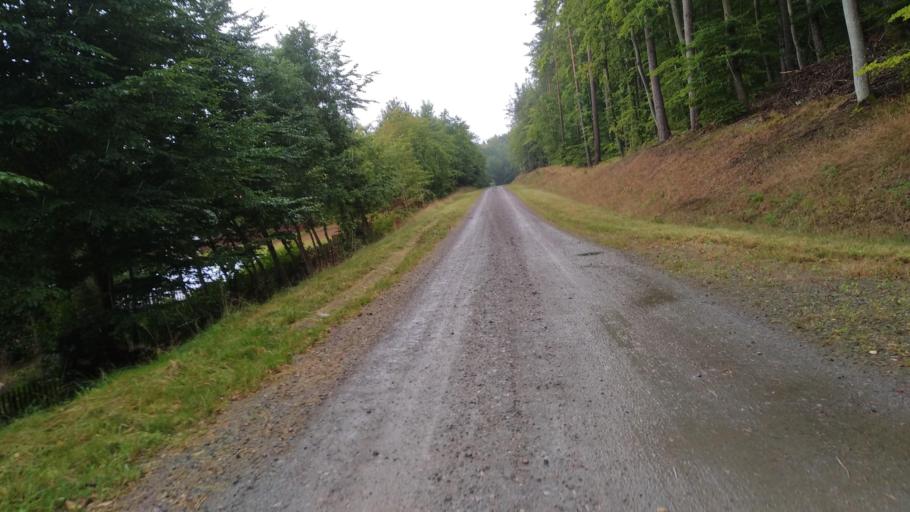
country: PL
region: Pomeranian Voivodeship
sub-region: Powiat wejherowski
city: Goscicino
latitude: 54.6299
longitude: 18.1383
